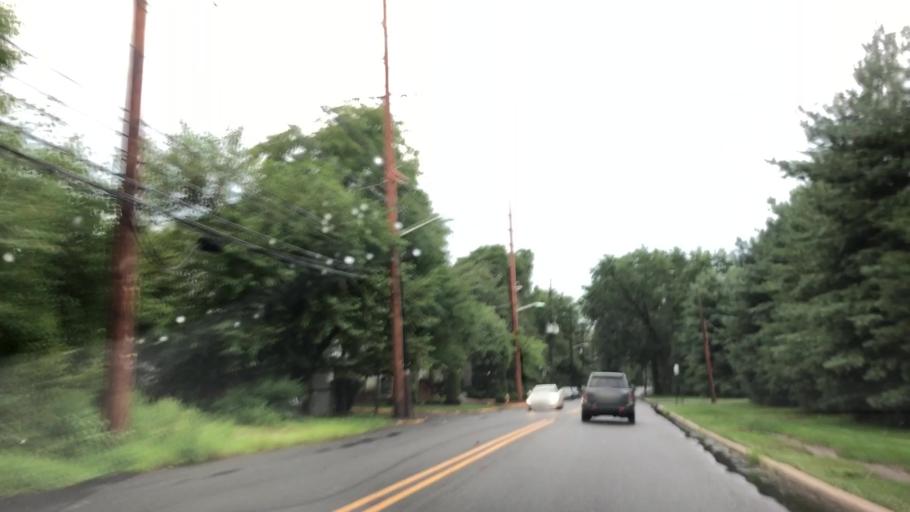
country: US
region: New Jersey
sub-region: Bergen County
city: Lyndhurst
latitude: 40.8211
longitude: -74.1355
